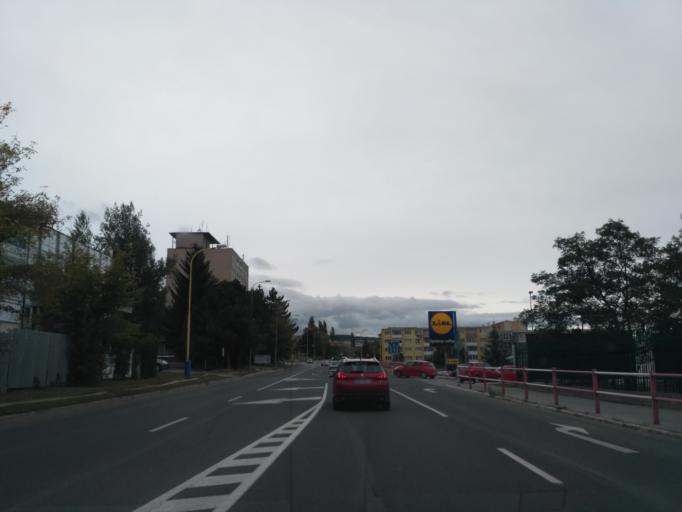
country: SK
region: Kosicky
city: Kosice
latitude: 48.7117
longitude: 21.2273
